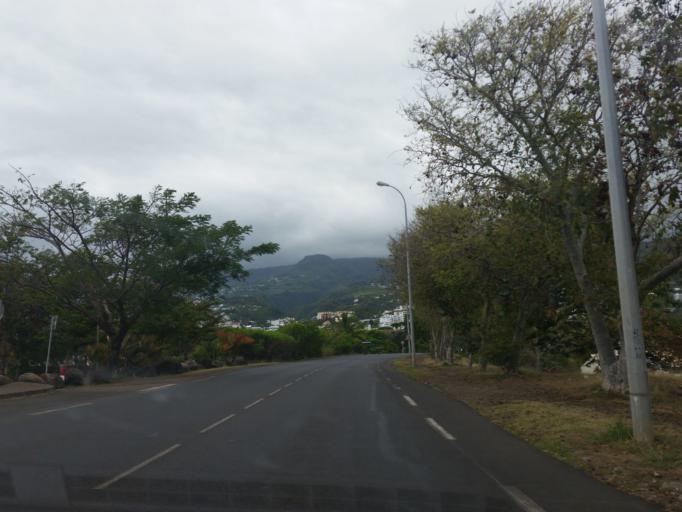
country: RE
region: Reunion
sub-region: Reunion
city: Saint-Denis
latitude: -20.8907
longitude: 55.4718
